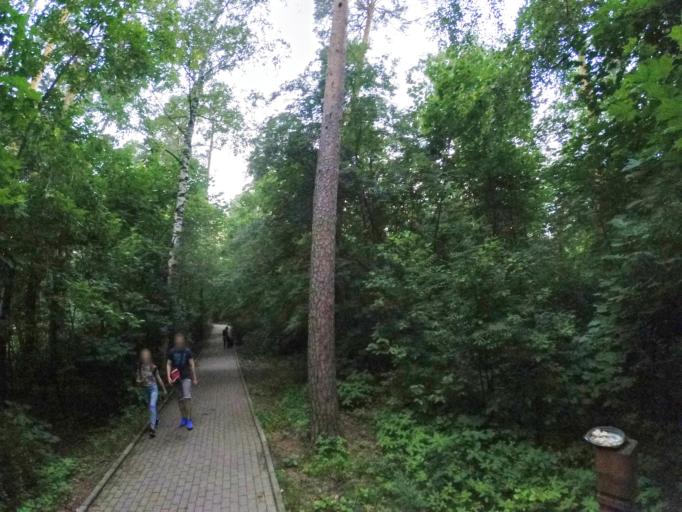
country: RU
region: Moscow
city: Shchukino
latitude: 55.7812
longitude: 37.4262
